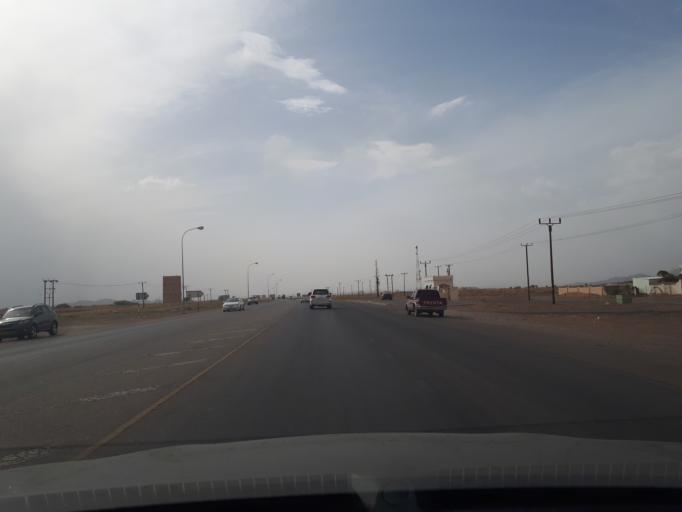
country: OM
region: Ash Sharqiyah
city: Badiyah
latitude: 22.5055
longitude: 58.7462
